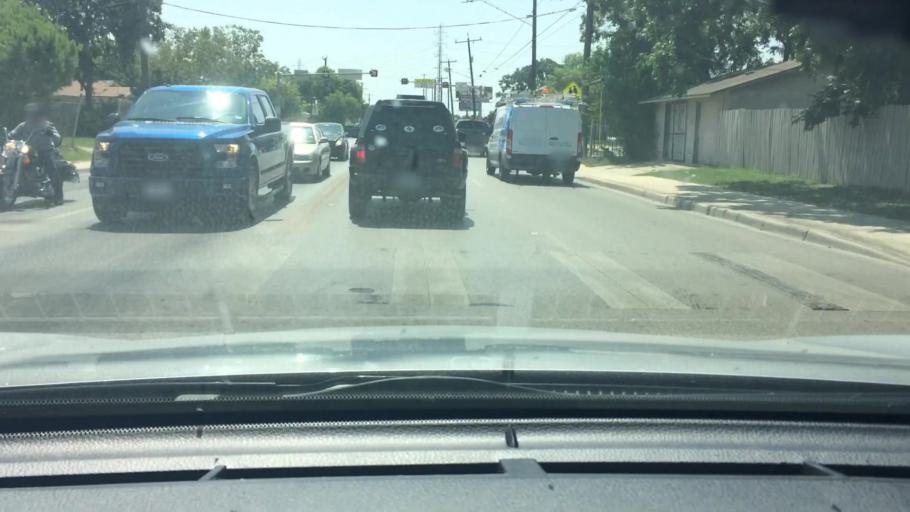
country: US
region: Texas
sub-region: Bexar County
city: San Antonio
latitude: 29.3633
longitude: -98.4391
